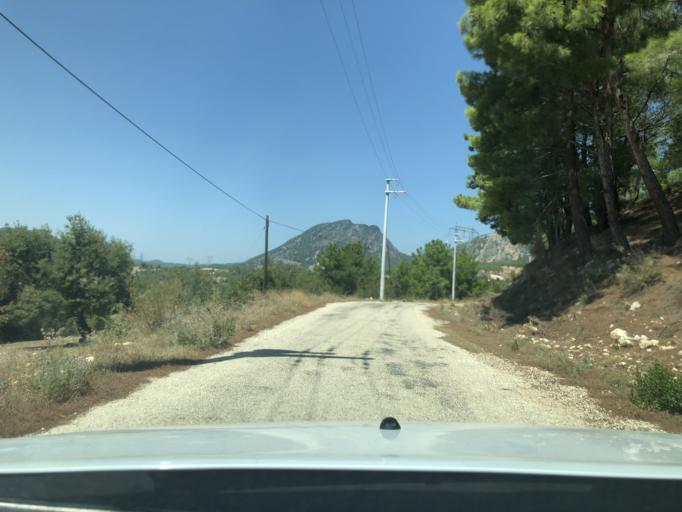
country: TR
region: Antalya
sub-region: Manavgat
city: Manavgat
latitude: 36.8736
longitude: 31.5502
